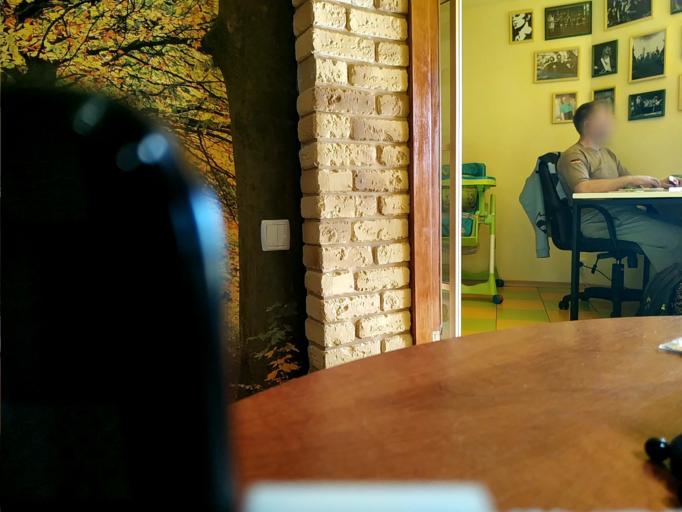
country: RU
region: Tverskaya
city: Vasil'yevskiy Mokh
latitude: 57.1418
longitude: 35.8423
